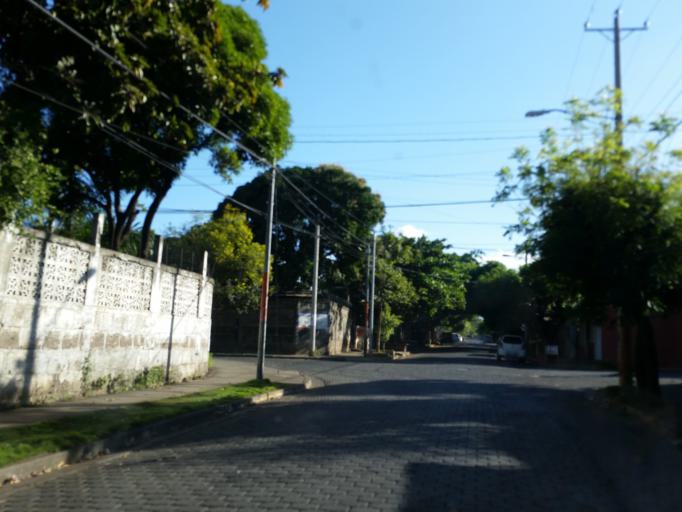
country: NI
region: Managua
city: Managua
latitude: 12.1189
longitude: -86.2946
